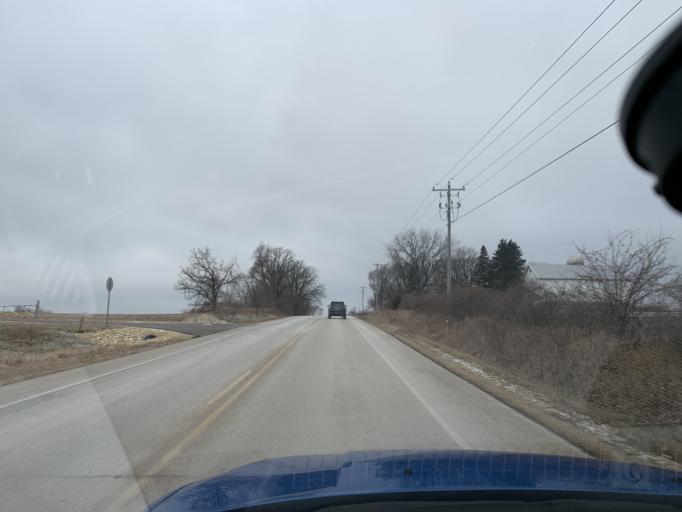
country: US
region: Wisconsin
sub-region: Dane County
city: Middleton
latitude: 43.0747
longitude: -89.5670
